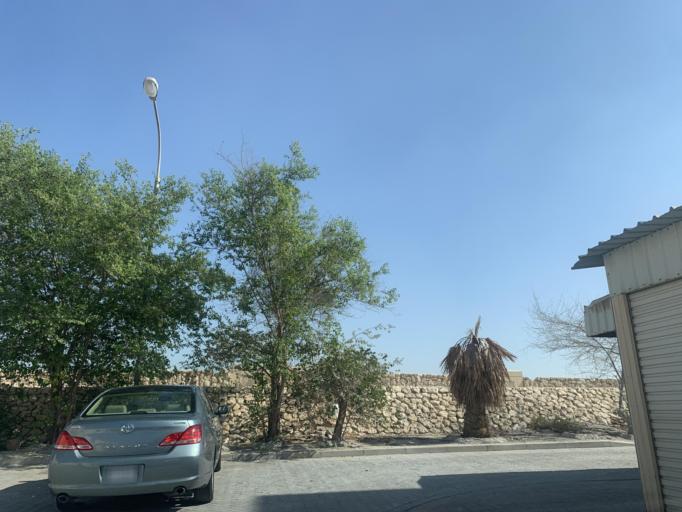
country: BH
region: Central Governorate
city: Madinat Hamad
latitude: 26.1199
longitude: 50.4965
